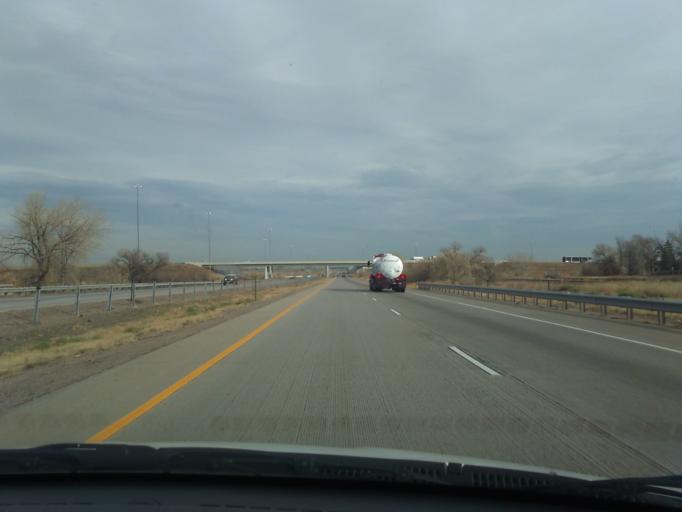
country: US
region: Colorado
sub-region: Adams County
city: Brighton
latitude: 39.9218
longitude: -104.8071
